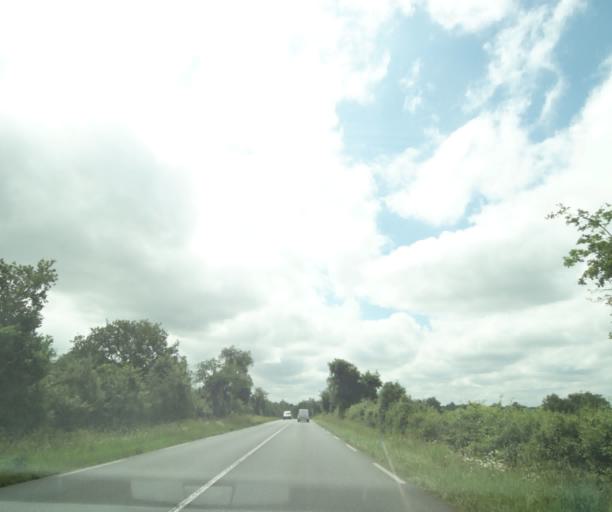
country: FR
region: Poitou-Charentes
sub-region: Departement des Deux-Sevres
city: Viennay
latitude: 46.7146
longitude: -0.2393
